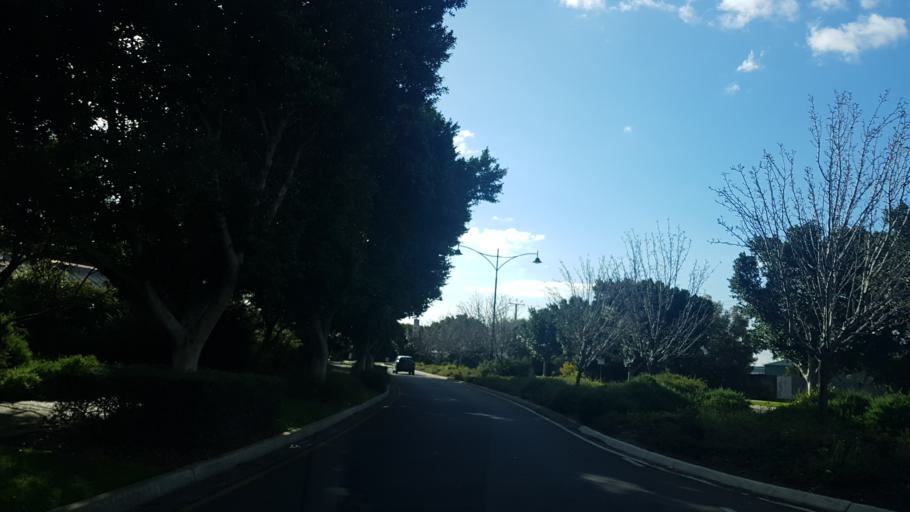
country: AU
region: South Australia
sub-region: Salisbury
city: Ingle Farm
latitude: -34.8240
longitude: 138.6138
